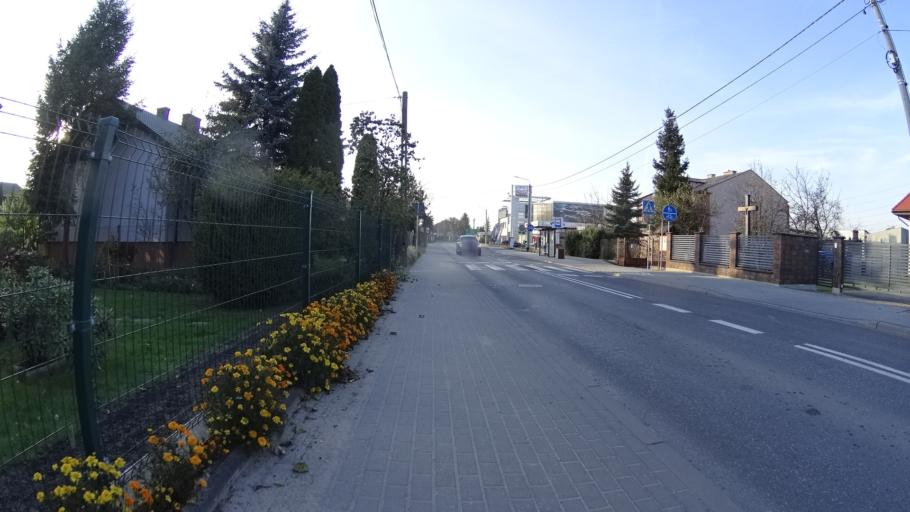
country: PL
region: Masovian Voivodeship
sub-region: Powiat warszawski zachodni
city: Babice
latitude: 52.2879
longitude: 20.8719
